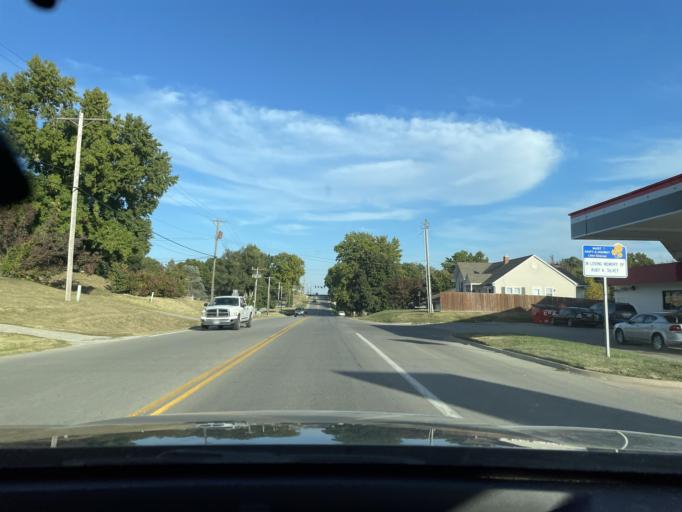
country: US
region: Missouri
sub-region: Buchanan County
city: Saint Joseph
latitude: 39.7552
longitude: -94.8012
